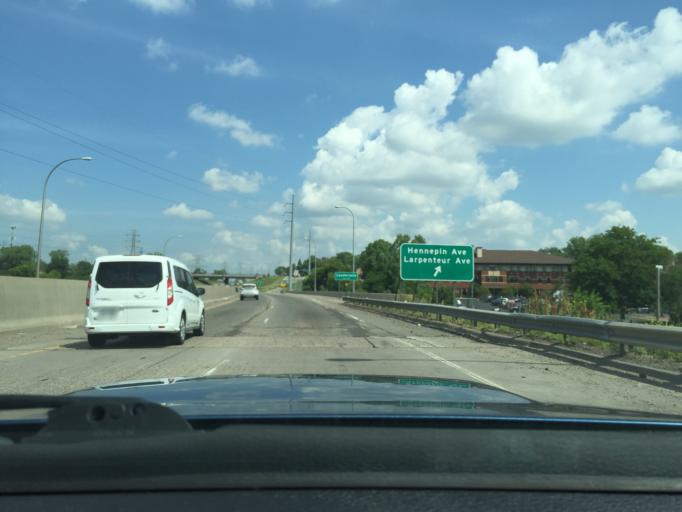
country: US
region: Minnesota
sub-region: Ramsey County
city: Lauderdale
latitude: 44.9876
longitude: -93.2035
